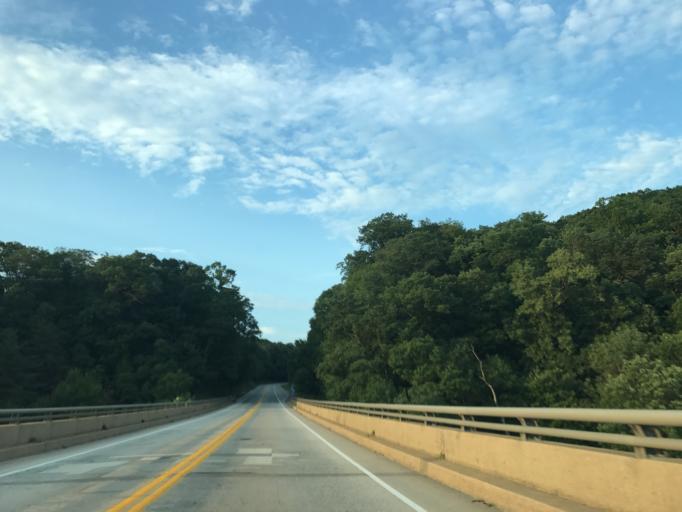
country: US
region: Pennsylvania
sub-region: York County
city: Susquehanna Trails
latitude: 39.8206
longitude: -76.3204
